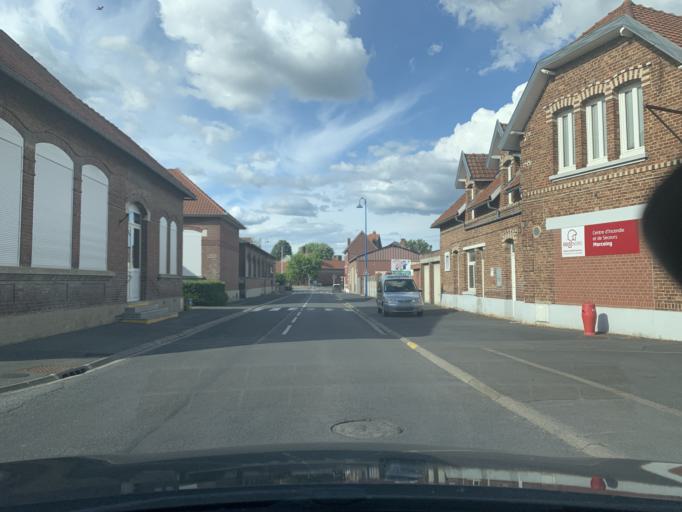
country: FR
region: Nord-Pas-de-Calais
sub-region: Departement du Nord
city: Marcoing
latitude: 50.1206
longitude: 3.1721
